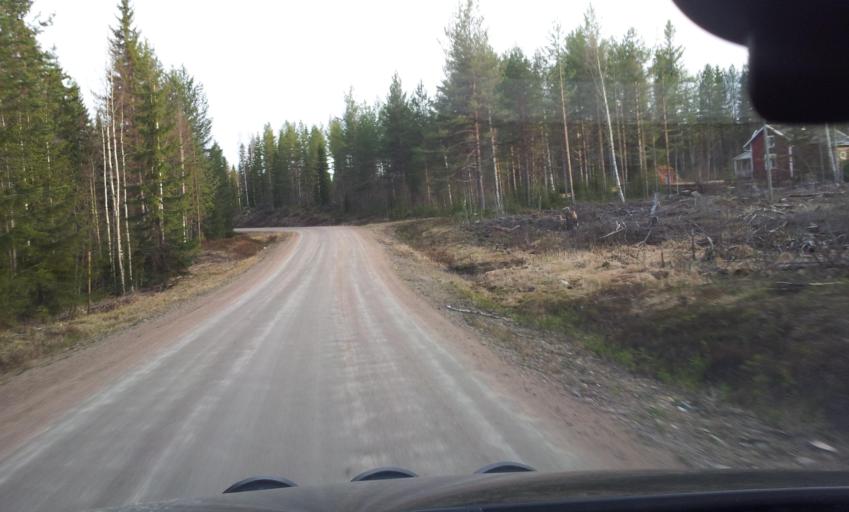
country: SE
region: Vaesternorrland
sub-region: Ange Kommun
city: Ange
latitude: 62.1401
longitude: 15.6604
